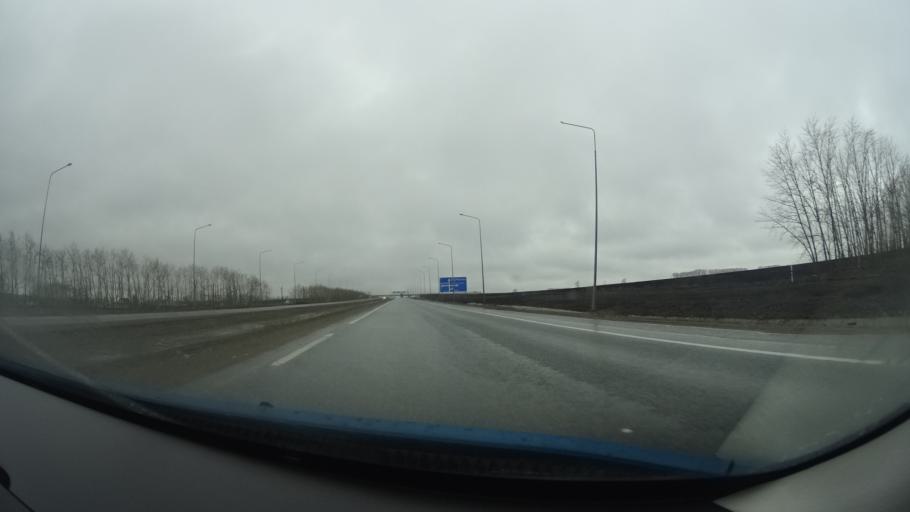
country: RU
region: Bashkortostan
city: Buzdyak
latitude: 54.7125
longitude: 54.8806
